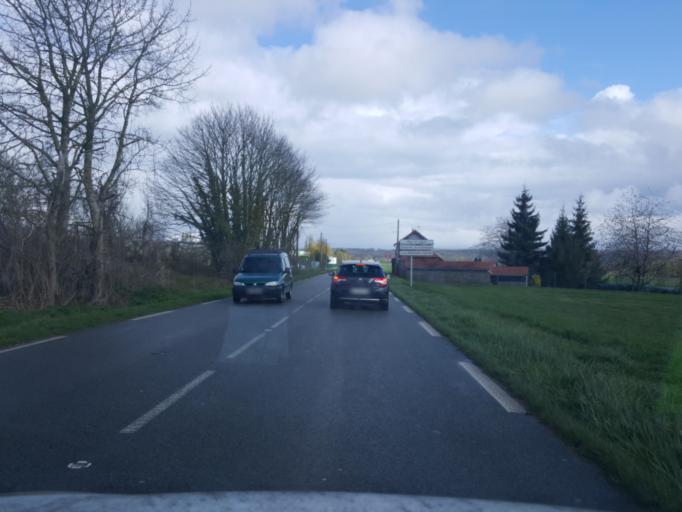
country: FR
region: Picardie
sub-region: Departement de l'Oise
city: Auneuil
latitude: 49.3803
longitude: 1.9959
